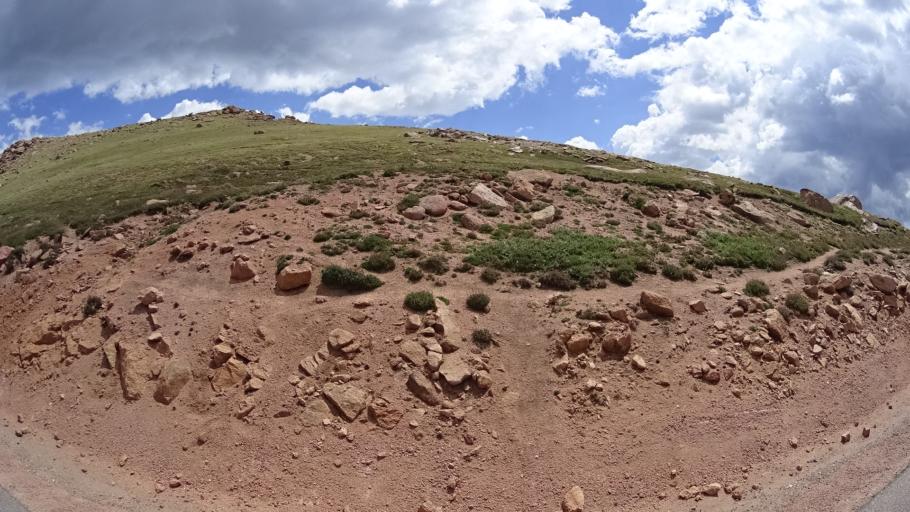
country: US
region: Colorado
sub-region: El Paso County
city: Cascade-Chipita Park
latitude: 38.8601
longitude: -105.0679
